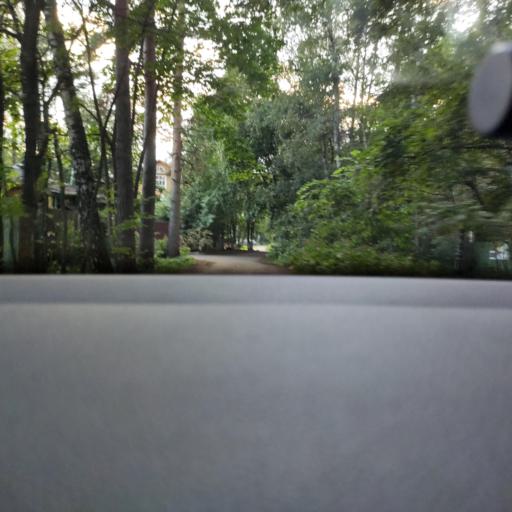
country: RU
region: Moscow
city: Novo-Peredelkino
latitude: 55.6501
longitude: 37.3168
